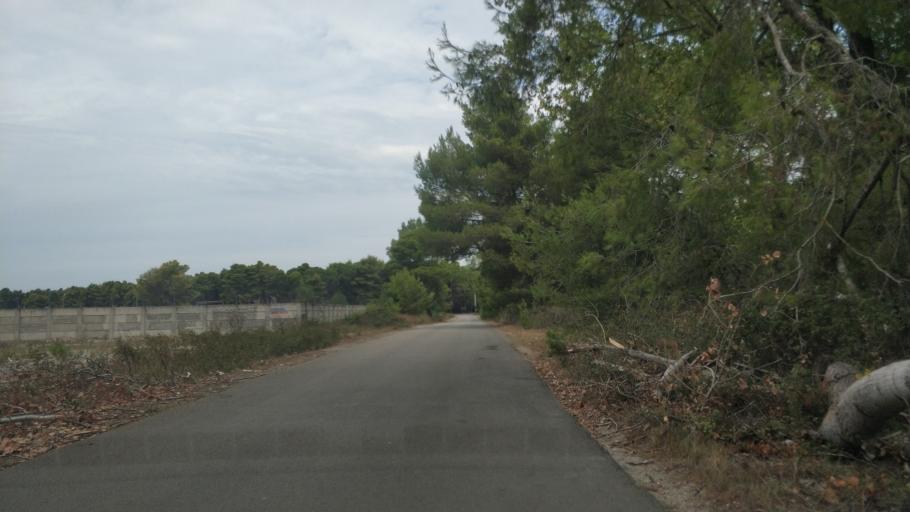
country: AL
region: Vlore
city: Vlore
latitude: 40.4907
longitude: 19.4385
